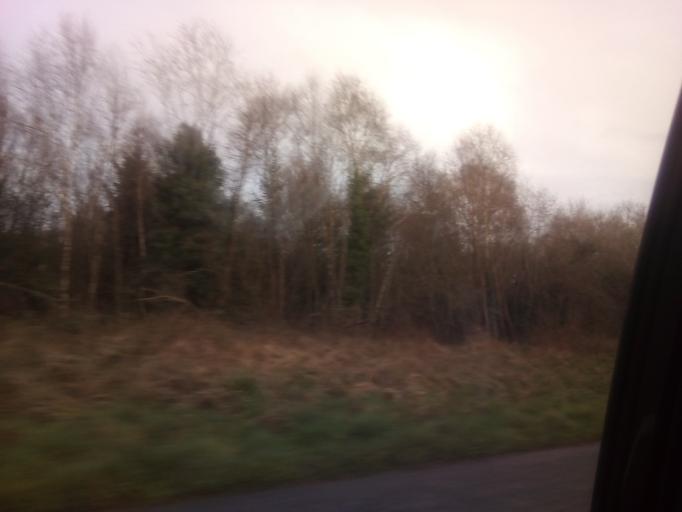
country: IE
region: Leinster
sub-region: Laois
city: Abbeyleix
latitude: 52.8979
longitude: -7.3591
